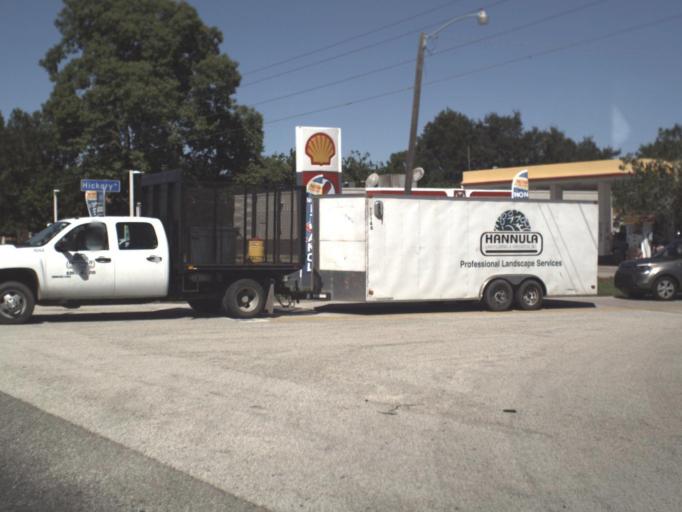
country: US
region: Florida
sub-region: Lee County
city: San Carlos Park
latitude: 26.4593
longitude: -81.8268
